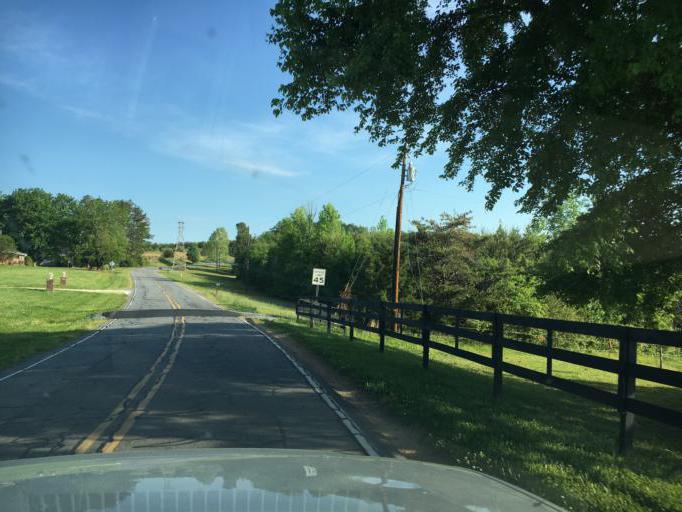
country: US
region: North Carolina
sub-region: Rutherford County
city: Rutherfordton
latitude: 35.3395
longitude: -81.9855
